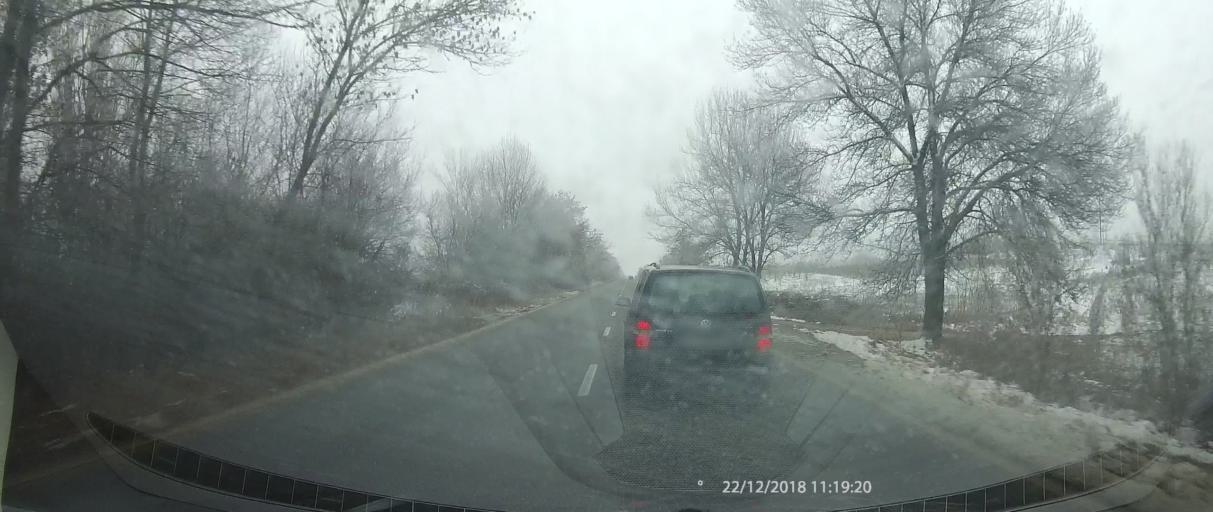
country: BG
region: Kyustendil
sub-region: Obshtina Kyustendil
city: Kyustendil
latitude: 42.2692
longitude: 22.7944
